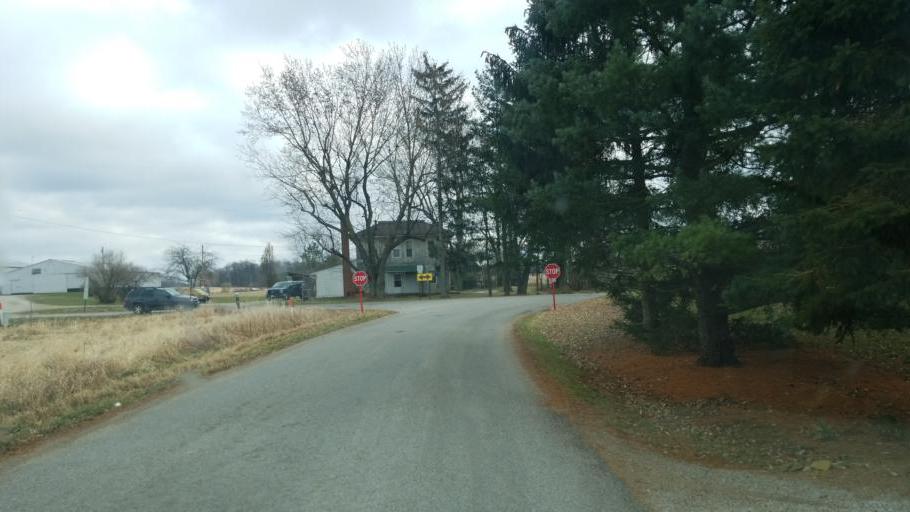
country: US
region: Ohio
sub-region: Richland County
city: Lexington
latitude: 40.6819
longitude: -82.6901
